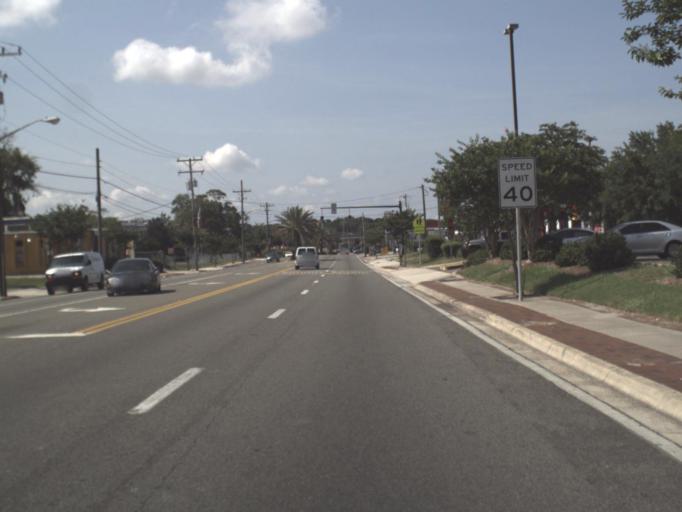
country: US
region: Florida
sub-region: Duval County
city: Jacksonville
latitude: 30.3336
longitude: -81.6030
